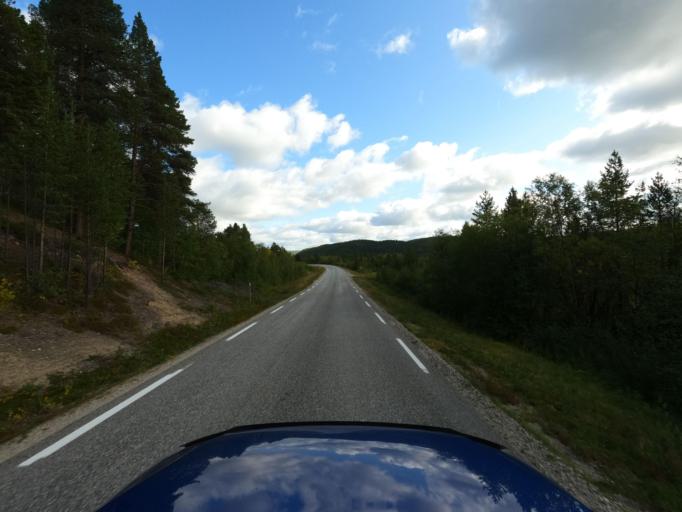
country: NO
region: Finnmark Fylke
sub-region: Karasjok
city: Karasjohka
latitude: 69.4333
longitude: 25.1443
